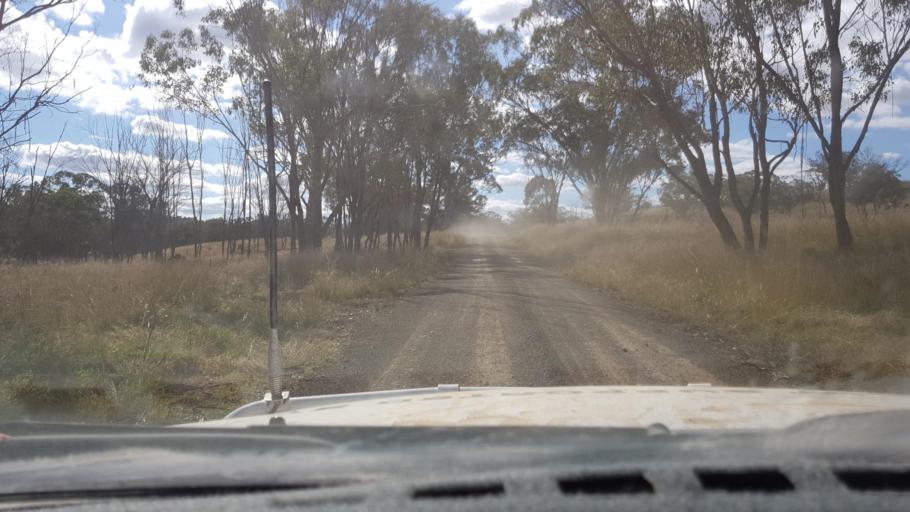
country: AU
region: New South Wales
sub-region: Tamworth Municipality
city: Manilla
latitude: -30.4661
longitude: 150.7777
